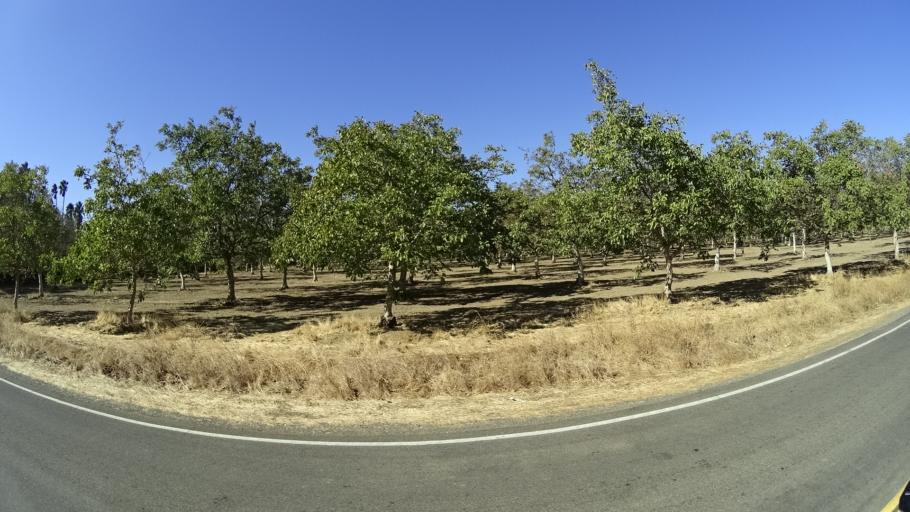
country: US
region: California
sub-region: Solano County
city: Dixon
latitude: 38.5337
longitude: -121.8498
